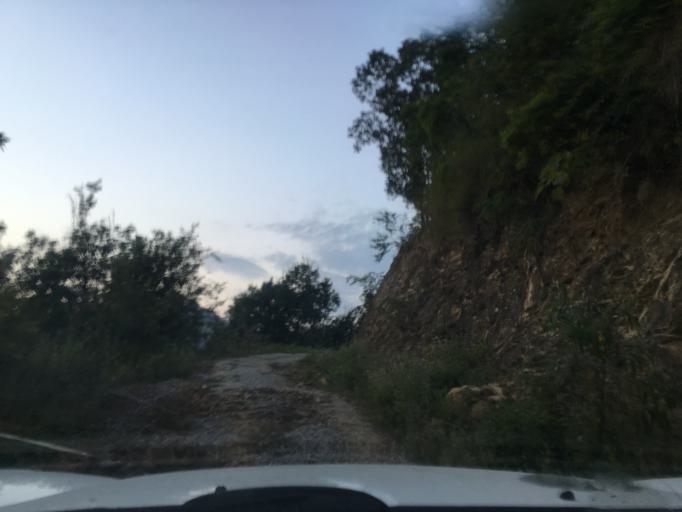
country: CN
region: Guangxi Zhuangzu Zizhiqu
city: Xinzhou
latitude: 25.3530
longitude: 105.7408
